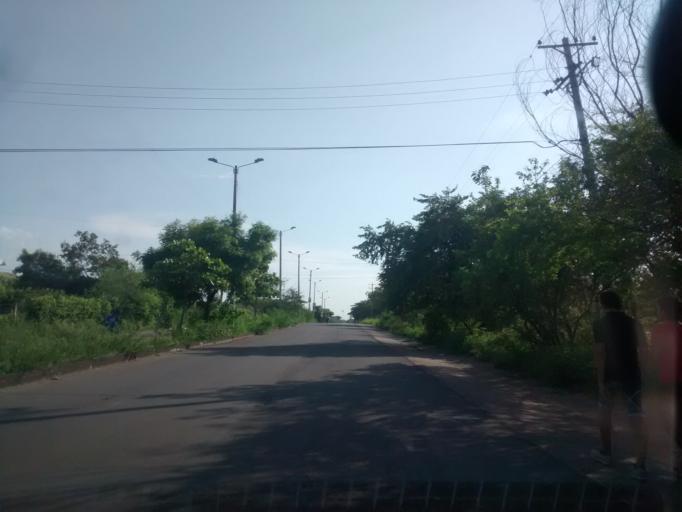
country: CO
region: Cundinamarca
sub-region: Girardot
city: Girardot City
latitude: 4.3162
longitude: -74.8079
